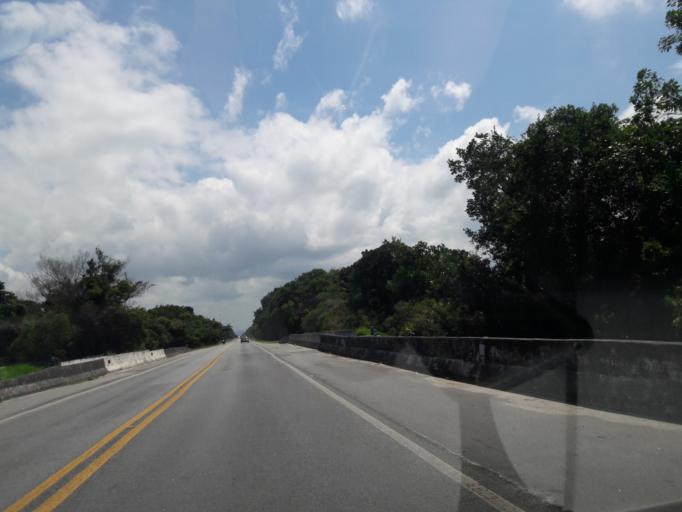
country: BR
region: Parana
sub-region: Pontal Do Parana
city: Pontal do Parana
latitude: -25.6878
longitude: -48.4899
